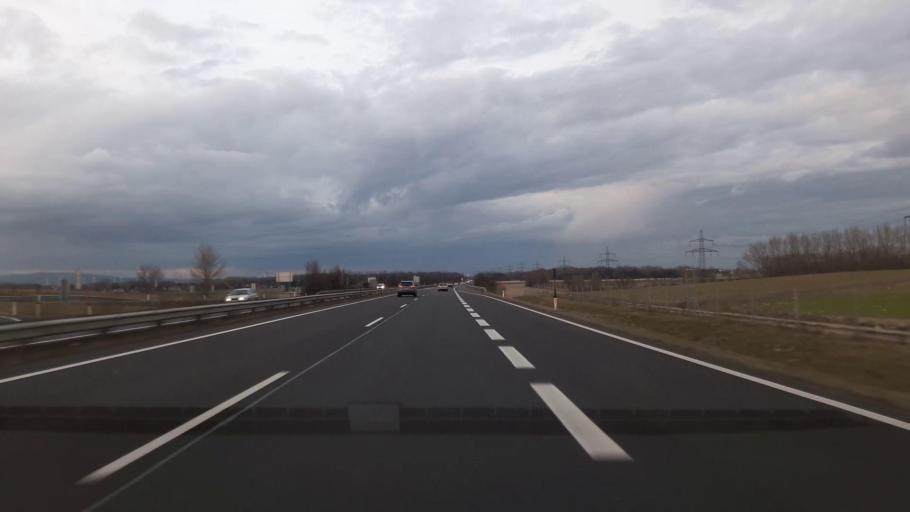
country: AT
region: Burgenland
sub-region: Eisenstadt-Umgebung
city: Hornstein
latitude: 47.8783
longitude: 16.4160
